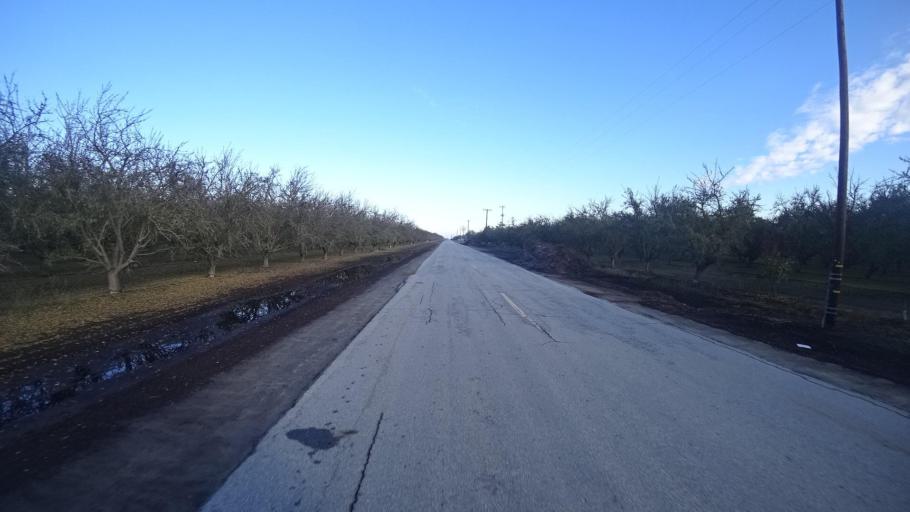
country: US
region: California
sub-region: Kern County
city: Delano
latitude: 35.7252
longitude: -119.3303
